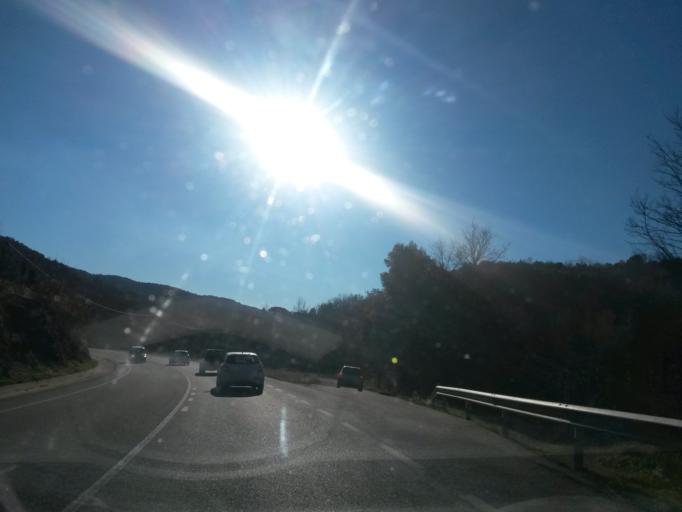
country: ES
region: Catalonia
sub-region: Provincia de Girona
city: Sant Feliu de Pallerols
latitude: 42.1047
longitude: 2.4923
